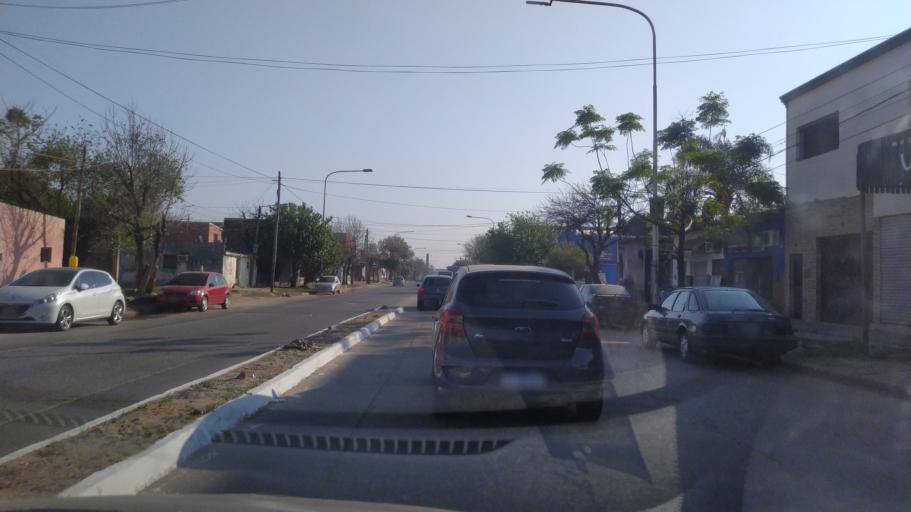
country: AR
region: Corrientes
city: Corrientes
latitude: -27.4825
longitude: -58.8155
